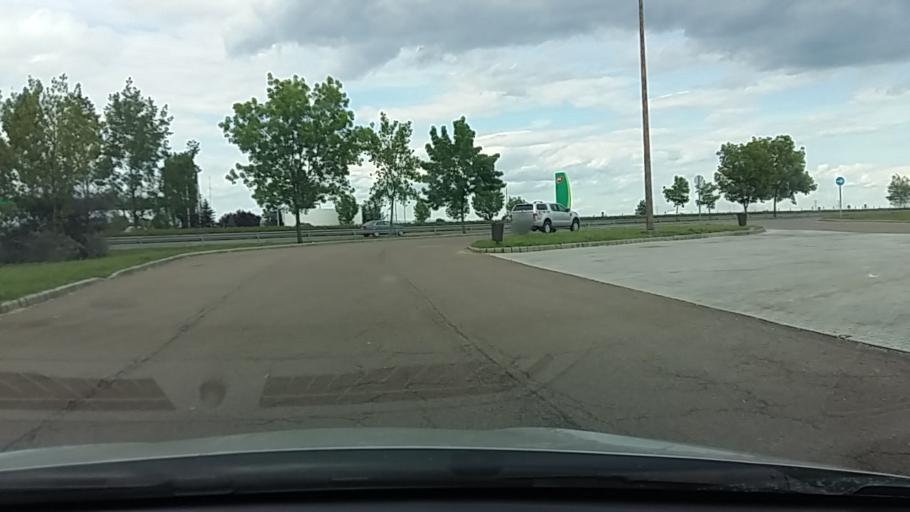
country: HU
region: Heves
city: Erdotelek
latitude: 47.7223
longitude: 20.3181
